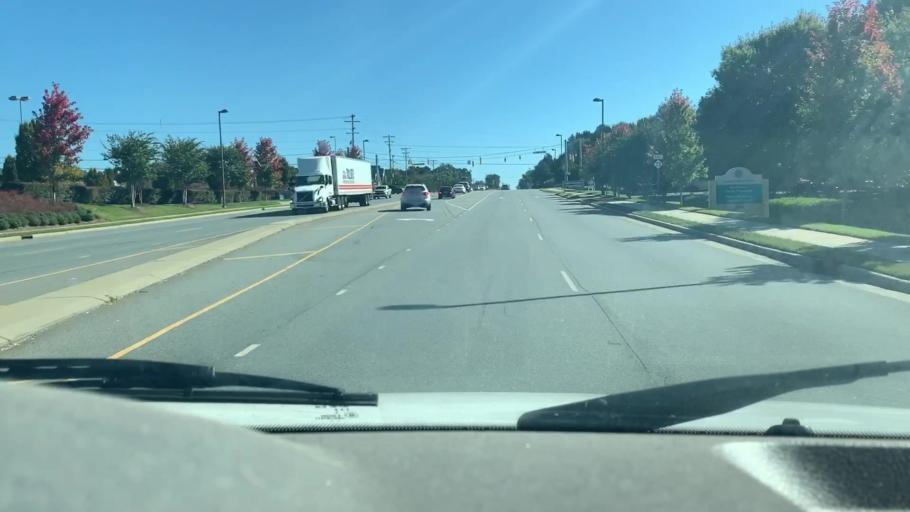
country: US
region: North Carolina
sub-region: Mecklenburg County
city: Huntersville
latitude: 35.4419
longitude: -80.8618
